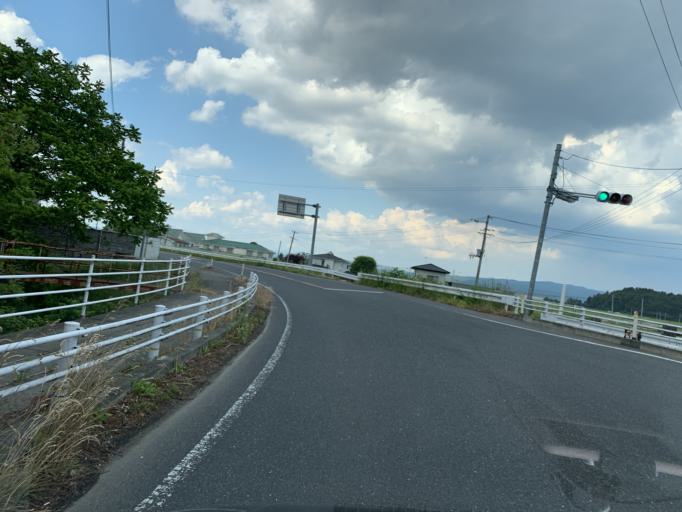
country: JP
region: Miyagi
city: Wakuya
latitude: 38.6478
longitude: 141.2169
